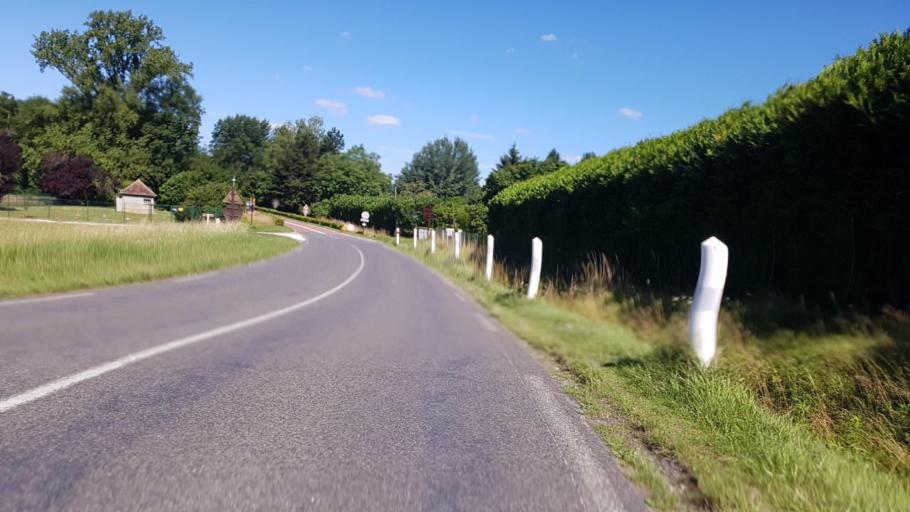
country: FR
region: Ile-de-France
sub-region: Departement de Seine-et-Marne
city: Saacy-sur-Marne
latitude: 48.9696
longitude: 3.1937
